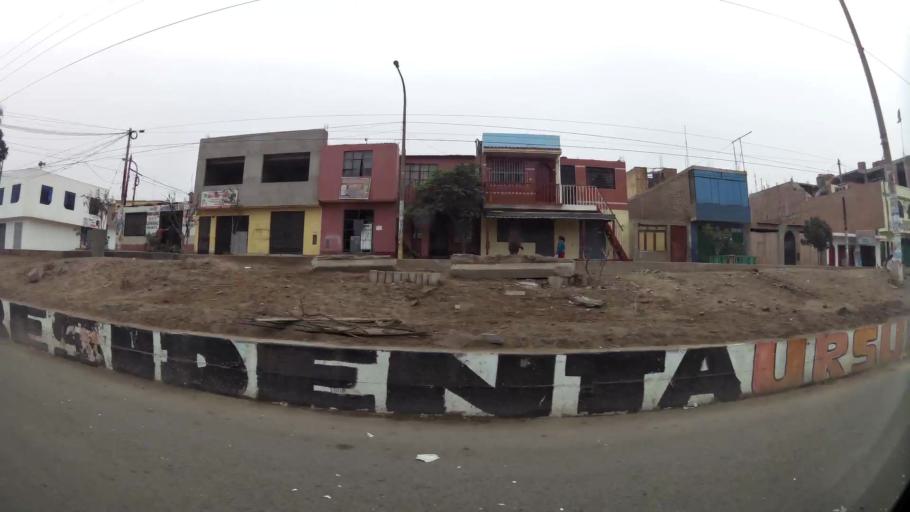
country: PE
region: Lima
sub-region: Lima
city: Santa Rosa
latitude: -11.8143
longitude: -77.1309
